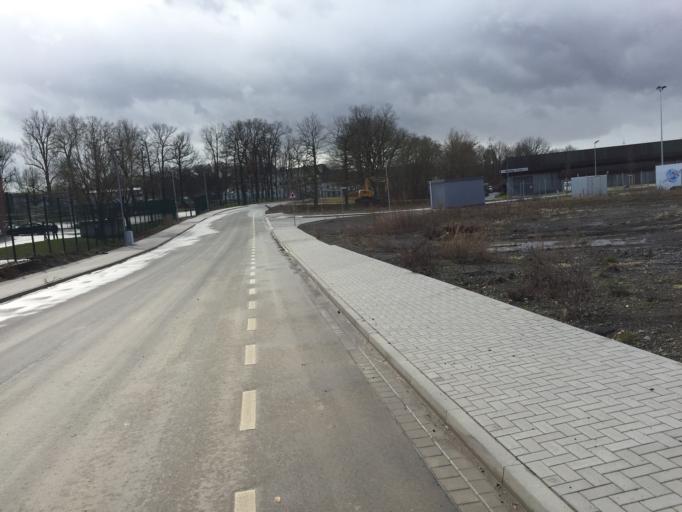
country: DE
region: Hesse
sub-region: Regierungsbezirk Giessen
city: Alten Buseck
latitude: 50.5946
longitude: 8.7312
